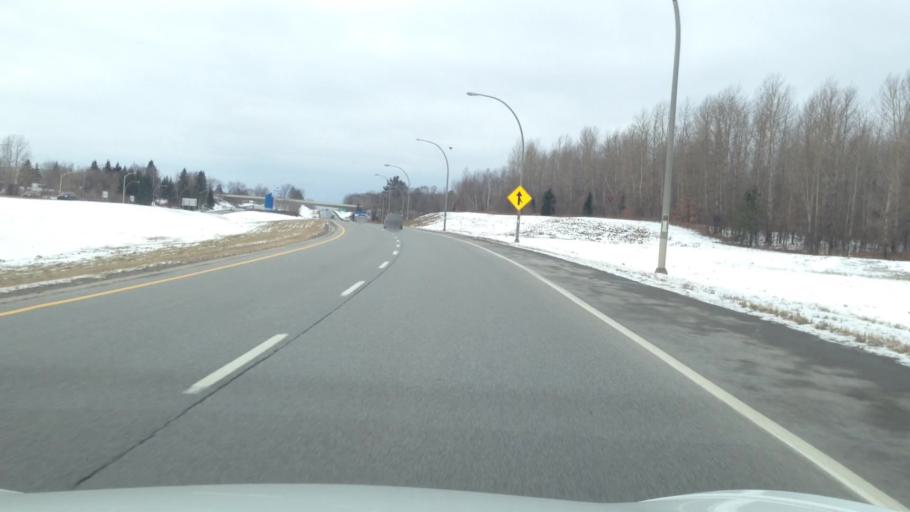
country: CA
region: Quebec
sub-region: Monteregie
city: Rigaud
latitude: 45.5376
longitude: -74.3834
